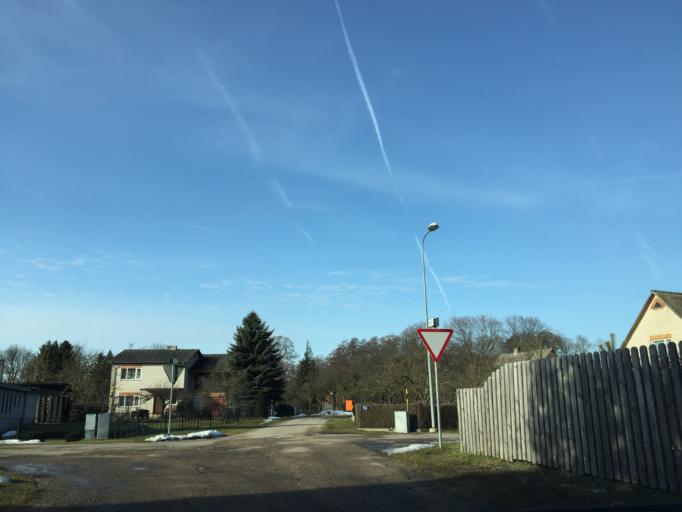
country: EE
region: Saare
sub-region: Kuressaare linn
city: Kuressaare
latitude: 58.3619
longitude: 22.0361
